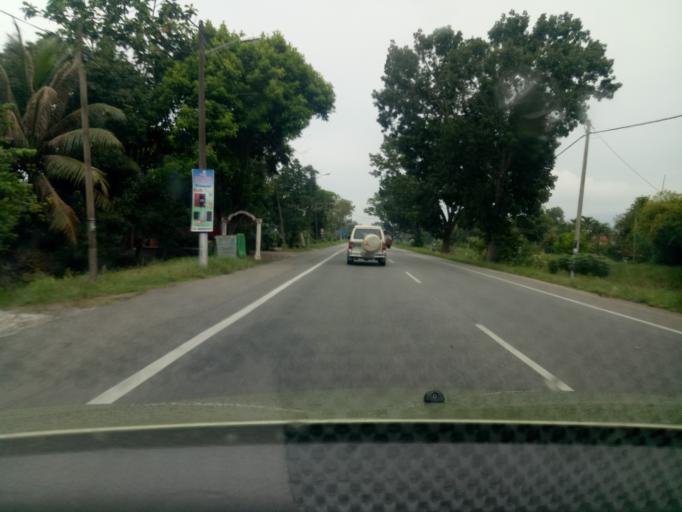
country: MY
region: Kedah
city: Gurun
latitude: 5.8893
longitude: 100.4421
